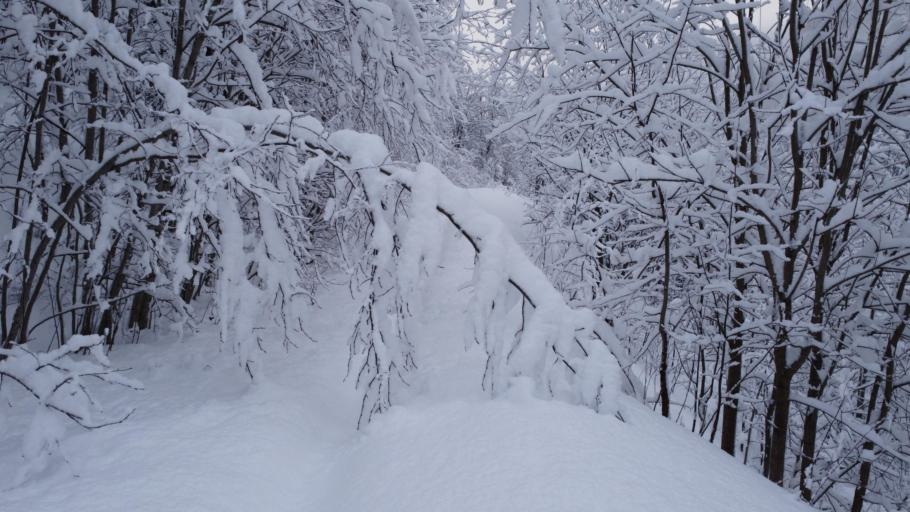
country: NO
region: Nordland
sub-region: Rana
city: Mo i Rana
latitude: 66.3321
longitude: 14.1646
